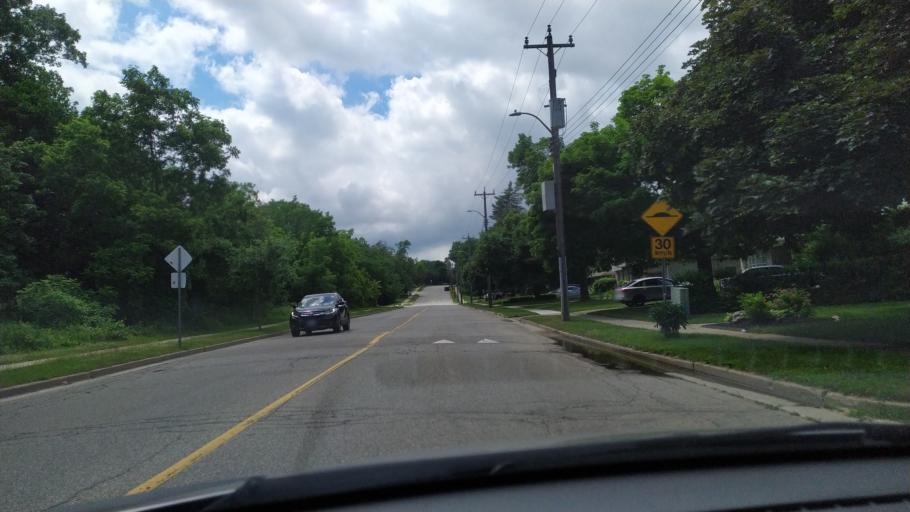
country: CA
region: Ontario
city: Kitchener
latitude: 43.4288
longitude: -80.5004
